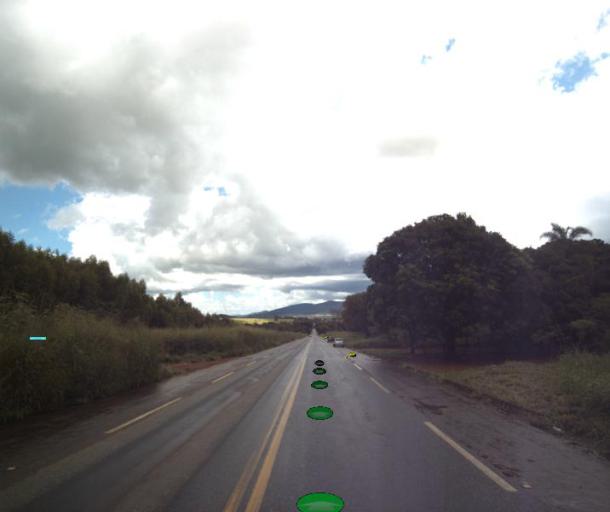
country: BR
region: Goias
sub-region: Pirenopolis
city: Pirenopolis
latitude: -16.0474
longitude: -49.0749
